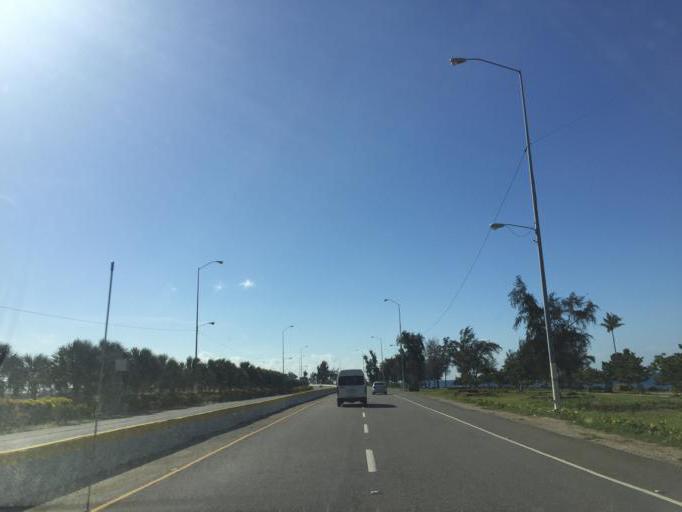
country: DO
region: Santo Domingo
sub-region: Santo Domingo
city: Boca Chica
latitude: 18.4439
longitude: -69.6812
